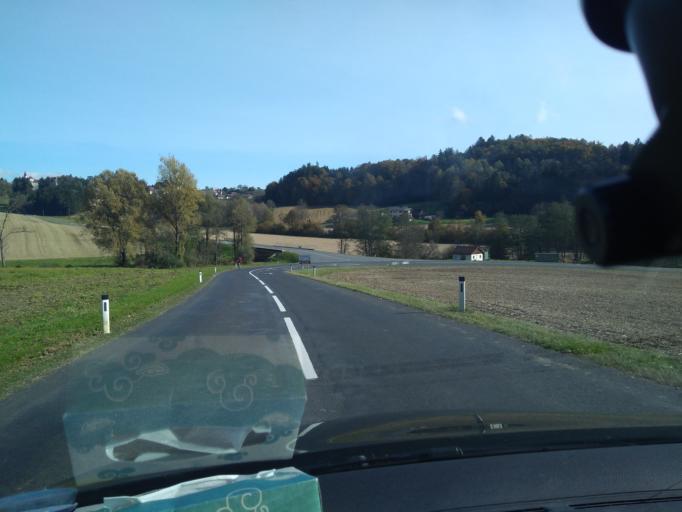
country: AT
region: Styria
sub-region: Politischer Bezirk Leibnitz
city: Sankt Ulrich am Waasen
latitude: 46.9130
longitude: 15.5339
